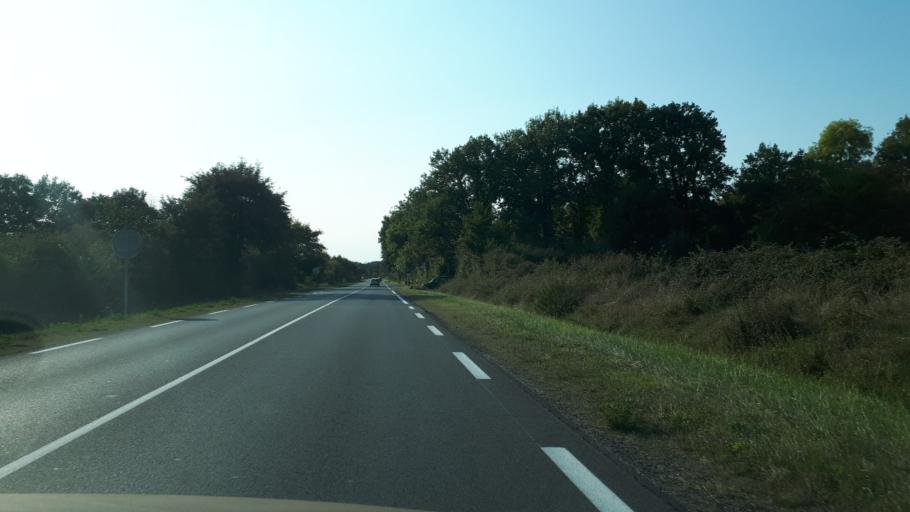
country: FR
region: Centre
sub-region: Departement du Cher
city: Vignoux-sur-Barangeon
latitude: 47.2127
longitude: 2.1319
